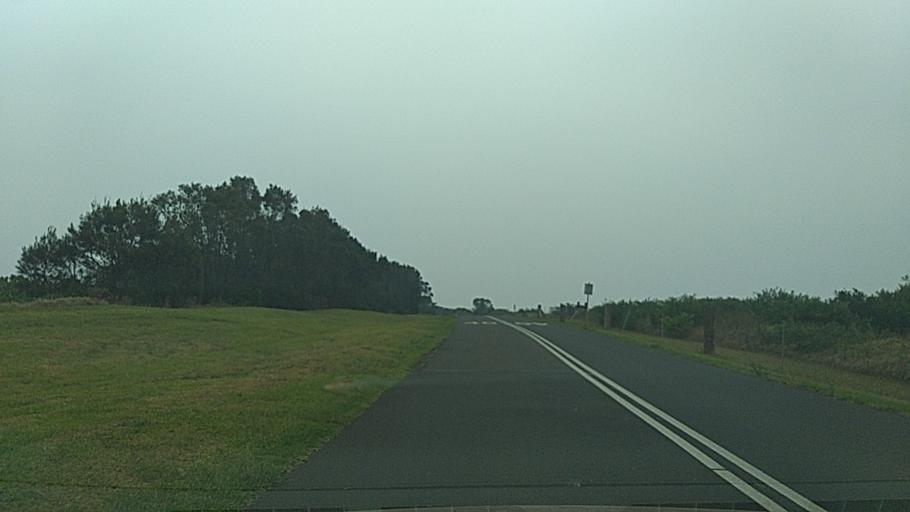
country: AU
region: New South Wales
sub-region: Shellharbour
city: Croom
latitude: -34.6086
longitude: 150.8603
